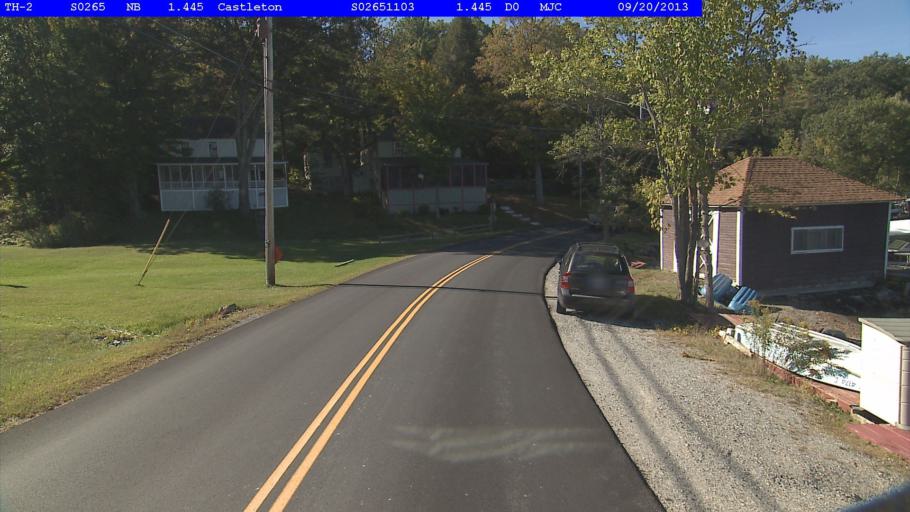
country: US
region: Vermont
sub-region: Rutland County
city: Fair Haven
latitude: 43.6238
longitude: -73.2323
